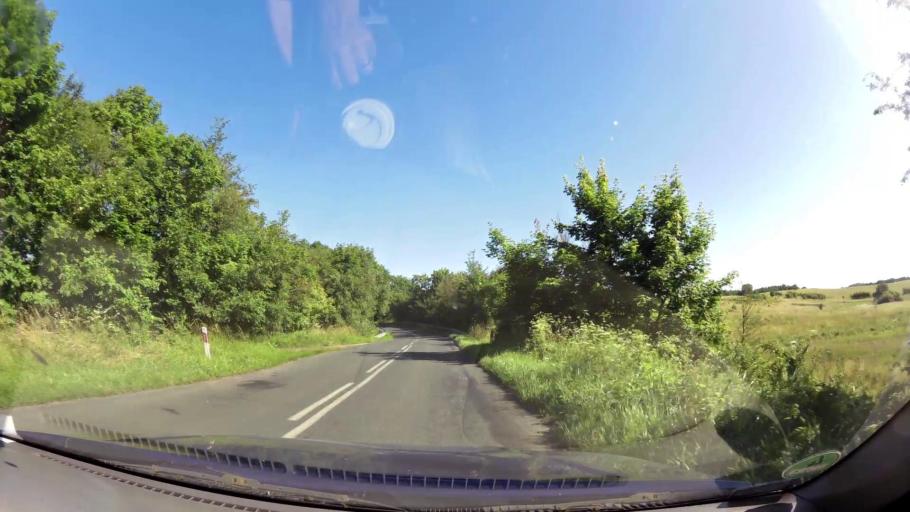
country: PL
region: West Pomeranian Voivodeship
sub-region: Powiat stargardzki
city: Dobrzany
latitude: 53.4214
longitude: 15.4257
